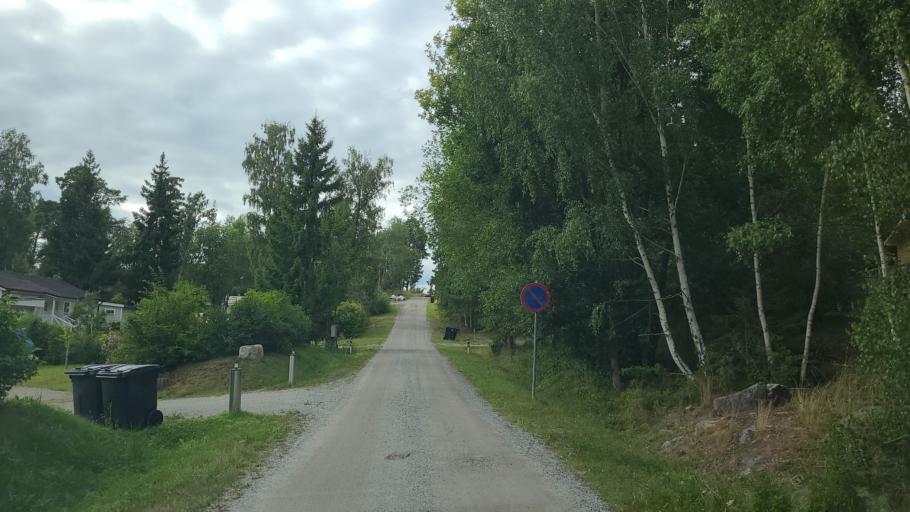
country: SE
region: Stockholm
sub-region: Upplands-Bro Kommun
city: Bro
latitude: 59.4750
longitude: 17.5502
